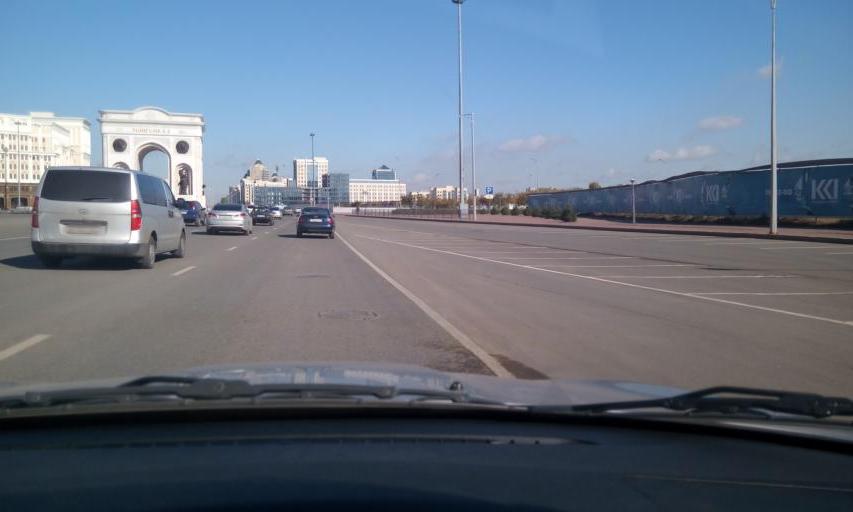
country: KZ
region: Astana Qalasy
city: Astana
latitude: 51.1026
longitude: 71.4296
